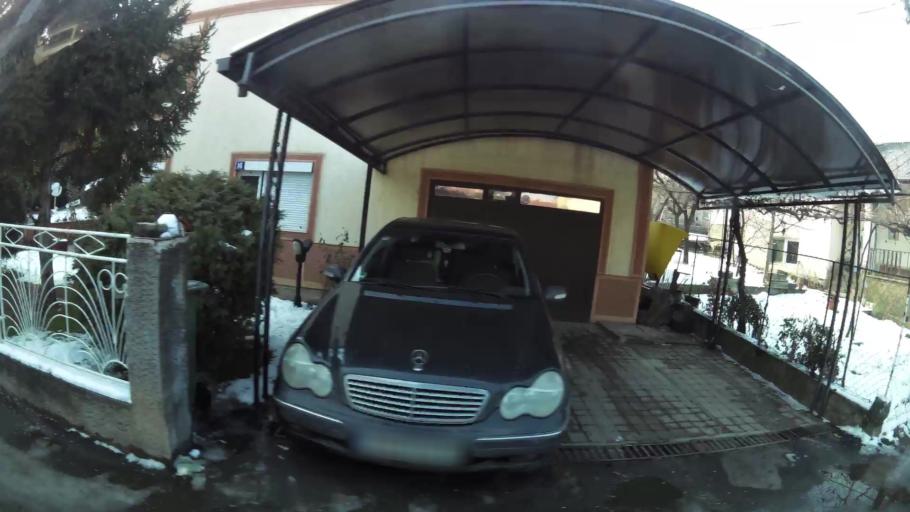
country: MK
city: Creshevo
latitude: 42.0097
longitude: 21.4993
